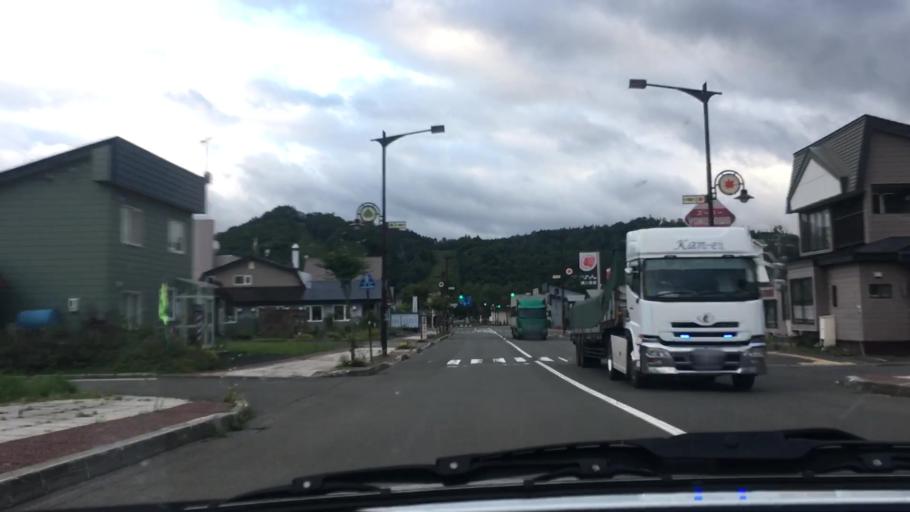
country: JP
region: Hokkaido
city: Shimo-furano
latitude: 42.9815
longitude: 142.3987
